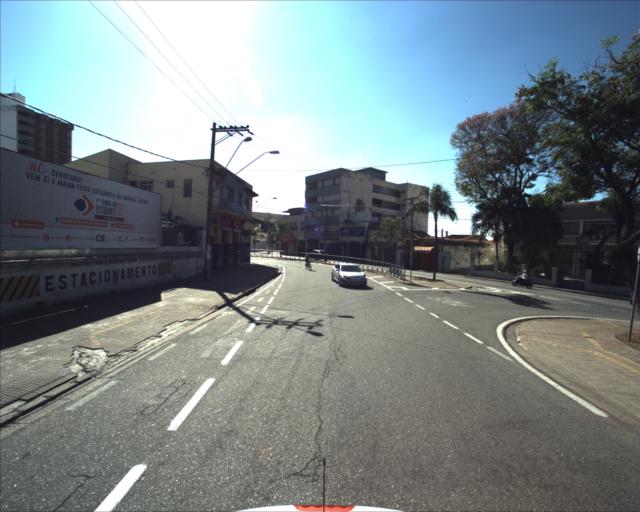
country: BR
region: Sao Paulo
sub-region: Sorocaba
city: Sorocaba
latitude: -23.4998
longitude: -47.4539
